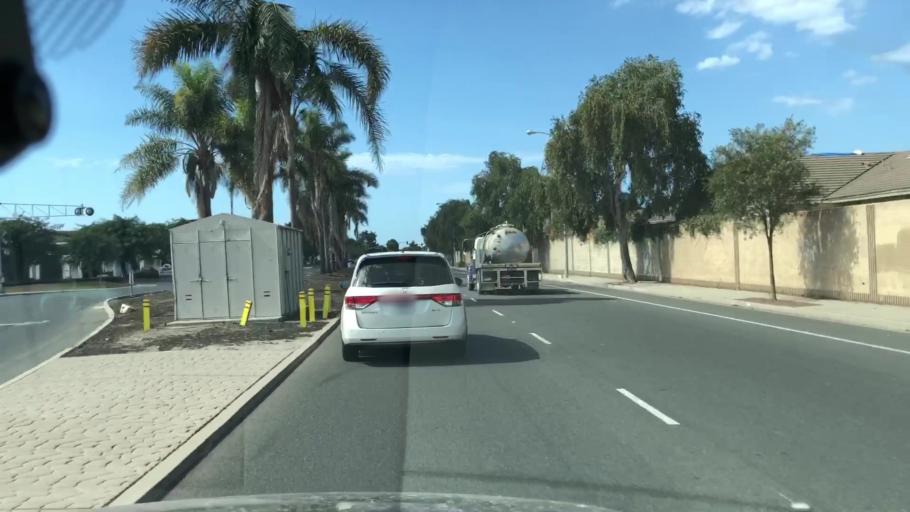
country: US
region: California
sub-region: Ventura County
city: Oxnard
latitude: 34.1904
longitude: -119.2041
